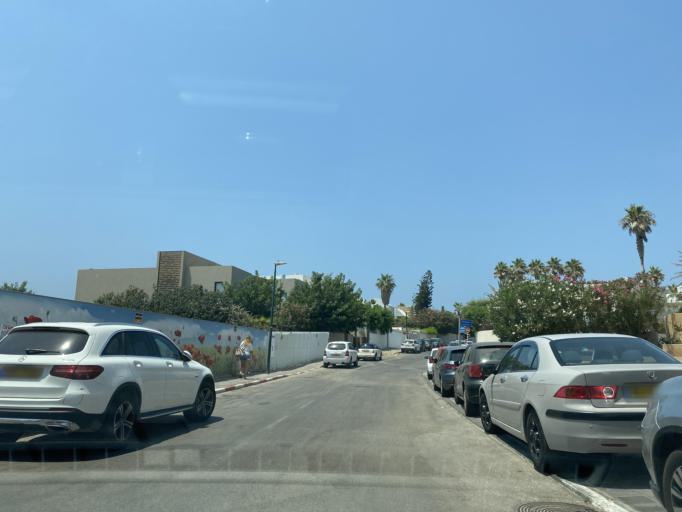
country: IL
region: Tel Aviv
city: Herzliya Pituah
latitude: 32.1800
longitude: 34.8043
